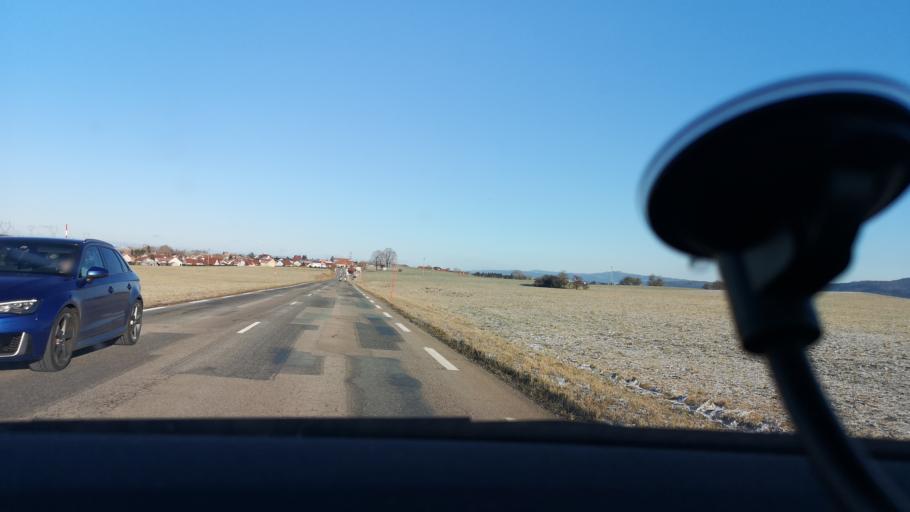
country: FR
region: Franche-Comte
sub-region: Departement du Doubs
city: Frasne
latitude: 46.8460
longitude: 6.1415
